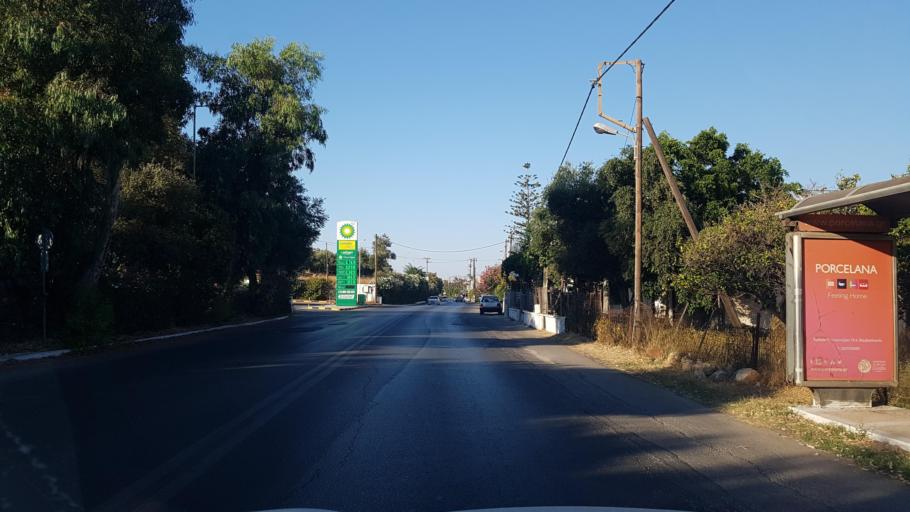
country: GR
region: Crete
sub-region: Nomos Chanias
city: Perivolia
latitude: 35.5006
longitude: 23.9984
